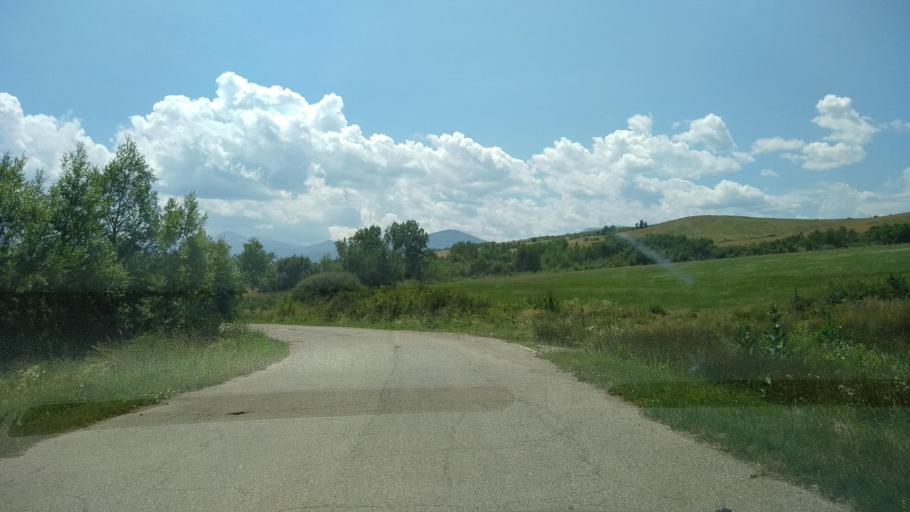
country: RO
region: Hunedoara
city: Densus
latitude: 45.5672
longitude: 22.8136
